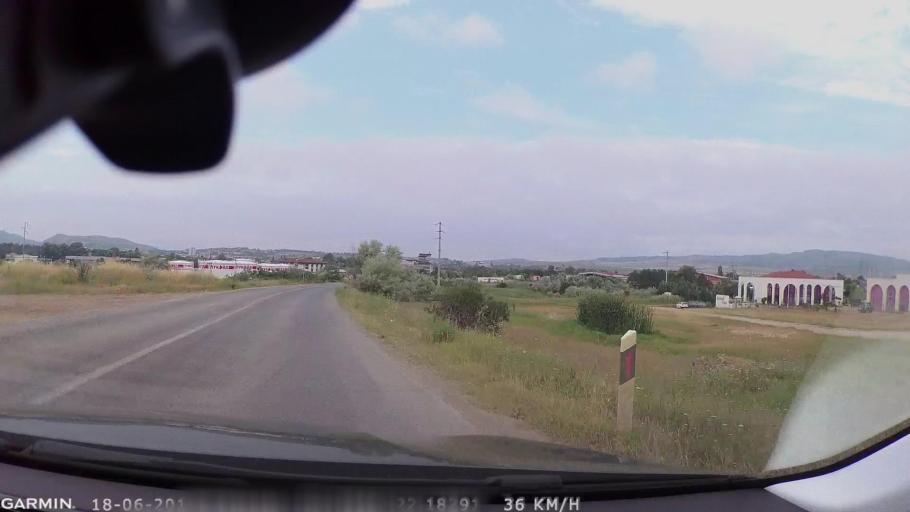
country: MK
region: Stip
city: Shtip
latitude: 41.7755
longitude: 22.1830
